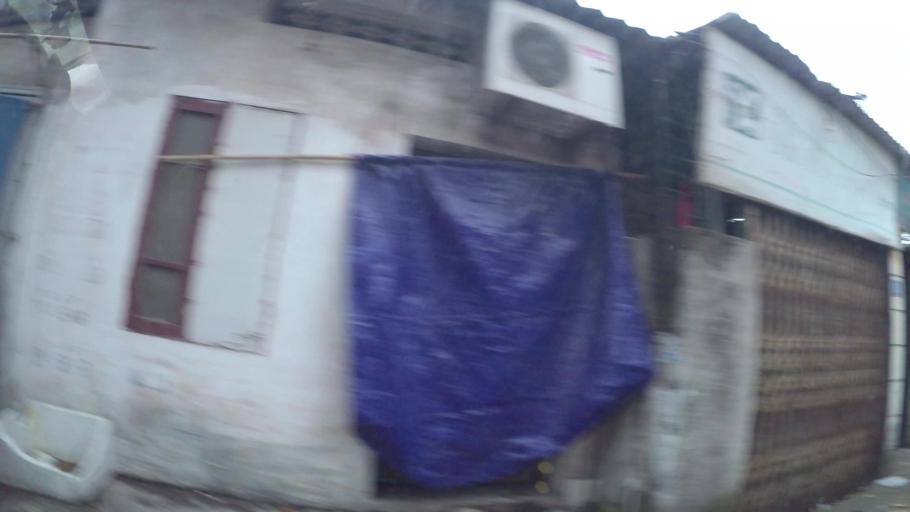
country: VN
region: Ha Noi
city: Hai BaTrung
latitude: 20.9959
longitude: 105.8758
